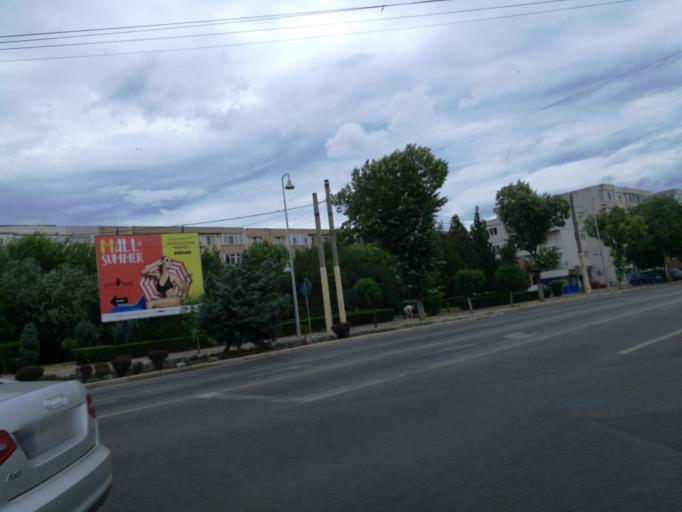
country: RO
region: Constanta
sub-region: Municipiul Constanta
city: Constanta
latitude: 44.1969
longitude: 28.6318
